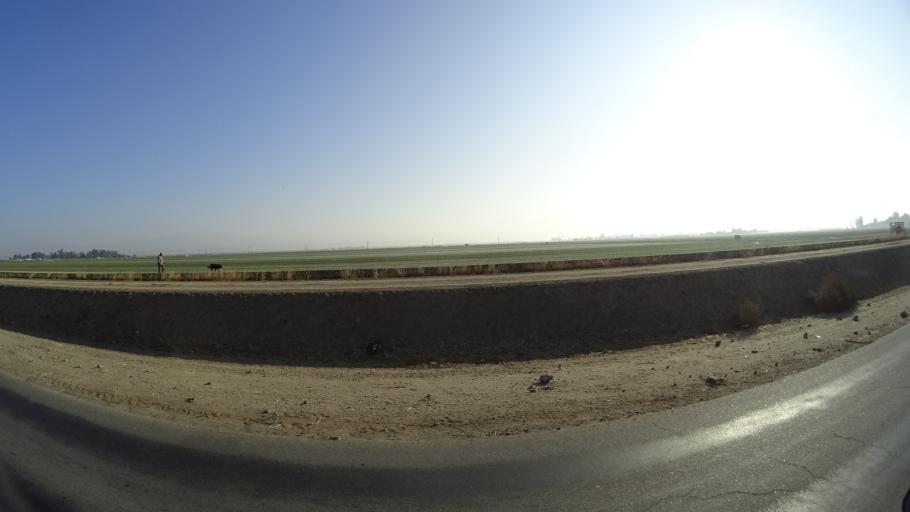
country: US
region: California
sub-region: Kern County
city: Greenfield
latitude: 35.2589
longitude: -118.9854
